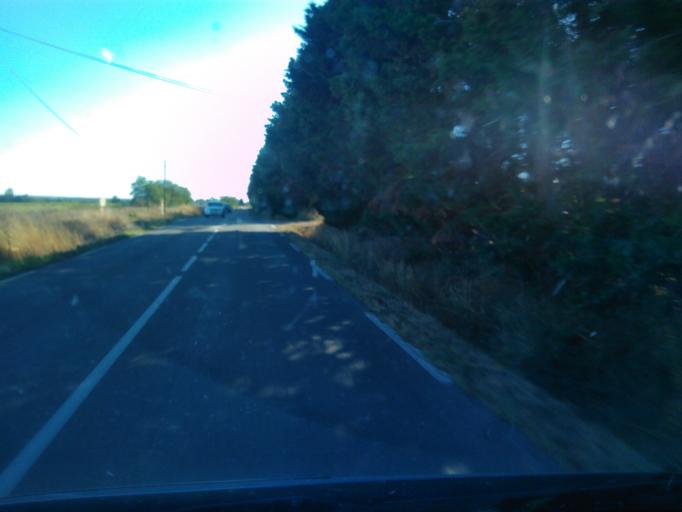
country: FR
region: Languedoc-Roussillon
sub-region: Departement du Gard
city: Beauvoisin
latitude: 43.6519
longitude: 4.3354
